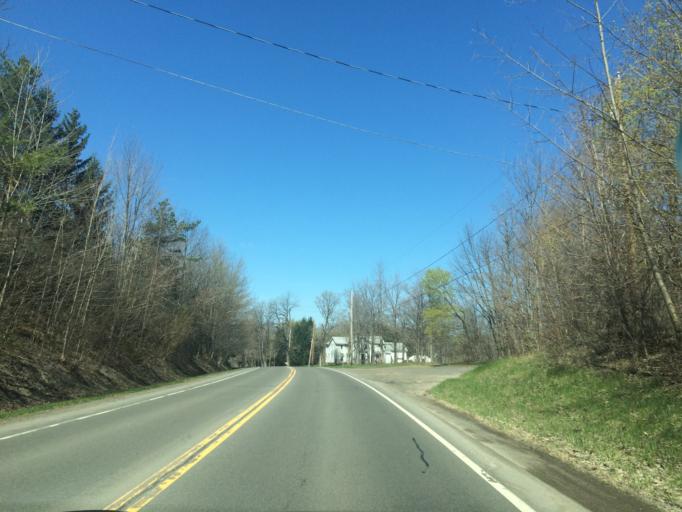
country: US
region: New York
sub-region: Wayne County
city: Macedon
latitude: 43.0957
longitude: -77.3617
